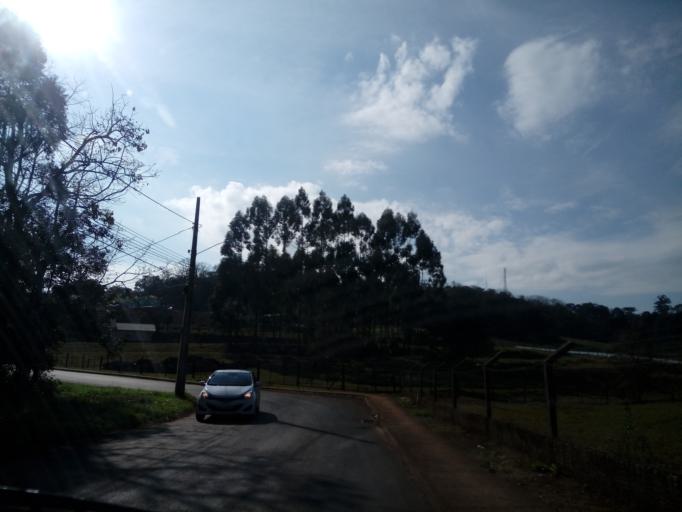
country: BR
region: Santa Catarina
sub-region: Chapeco
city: Chapeco
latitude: -27.1070
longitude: -52.5902
